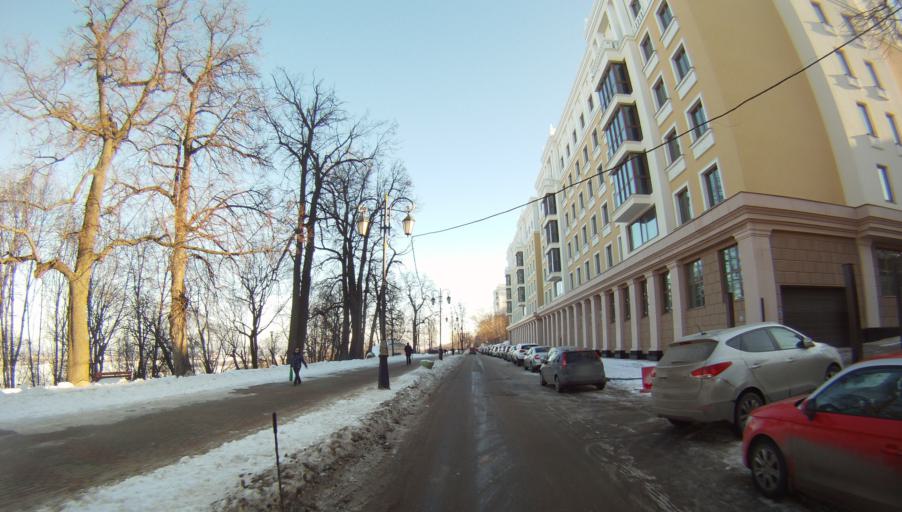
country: RU
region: Nizjnij Novgorod
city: Nizhniy Novgorod
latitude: 56.3285
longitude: 44.0206
